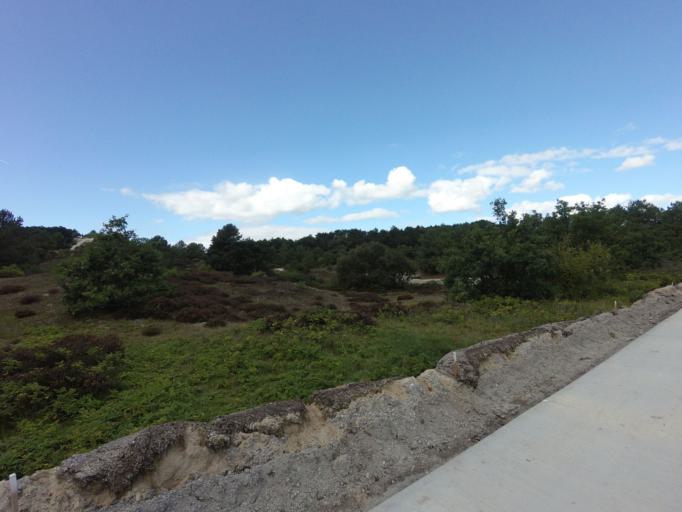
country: NL
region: North Holland
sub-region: Gemeente Bergen
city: Egmond aan Zee
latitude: 52.7165
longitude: 4.6628
